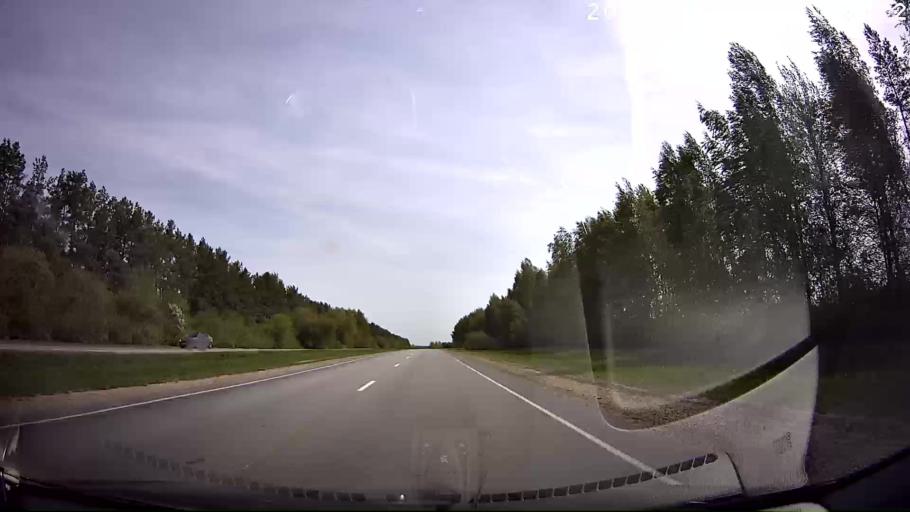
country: RU
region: Mariy-El
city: Sovetskiy
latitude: 56.7394
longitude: 48.1838
